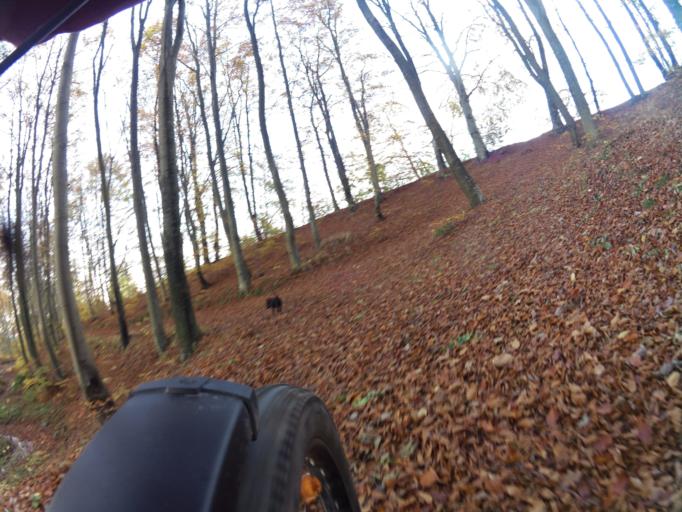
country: PL
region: Pomeranian Voivodeship
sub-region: Powiat pucki
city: Krokowa
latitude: 54.7720
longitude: 18.1729
